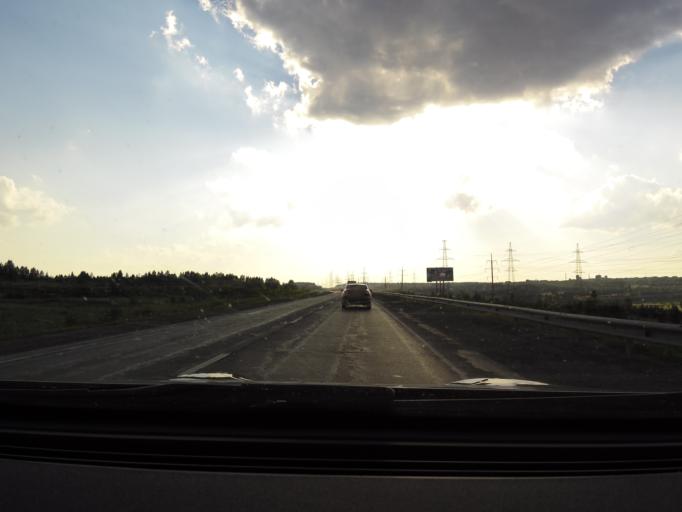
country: RU
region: Sverdlovsk
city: Revda
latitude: 56.8276
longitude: 59.9511
